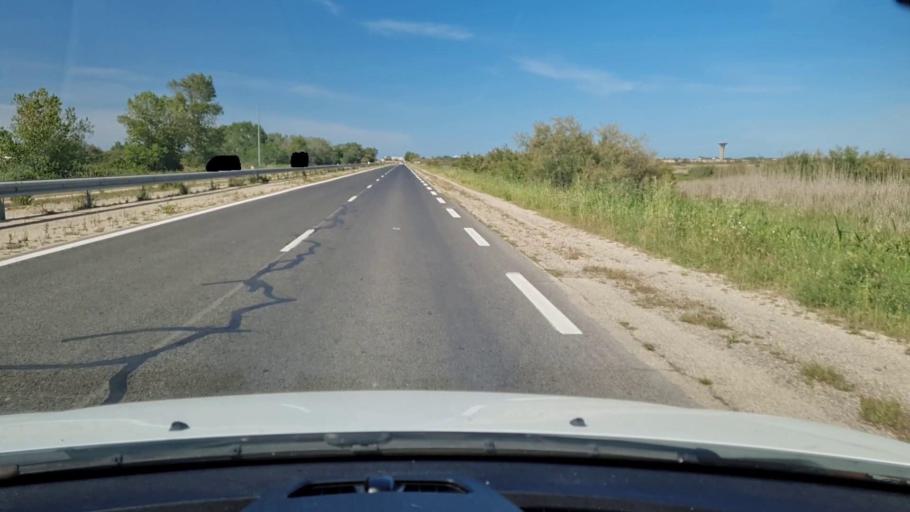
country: FR
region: Languedoc-Roussillon
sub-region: Departement du Gard
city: Le Grau-du-Roi
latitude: 43.5555
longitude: 4.1472
